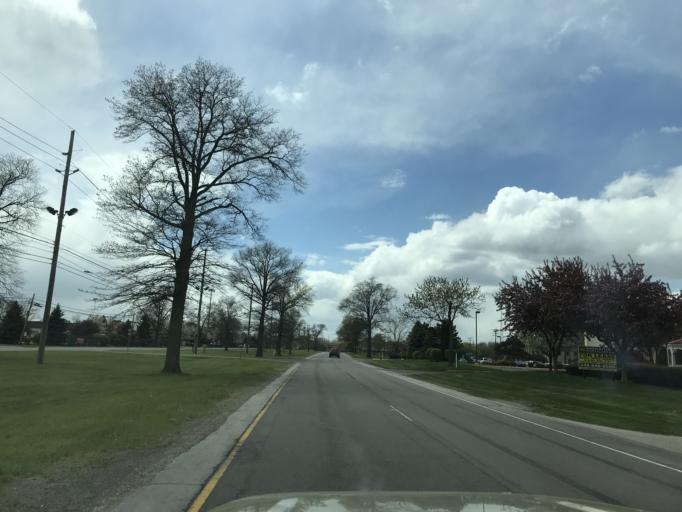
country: US
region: Michigan
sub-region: Wayne County
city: Plymouth
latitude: 42.3818
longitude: -83.4272
